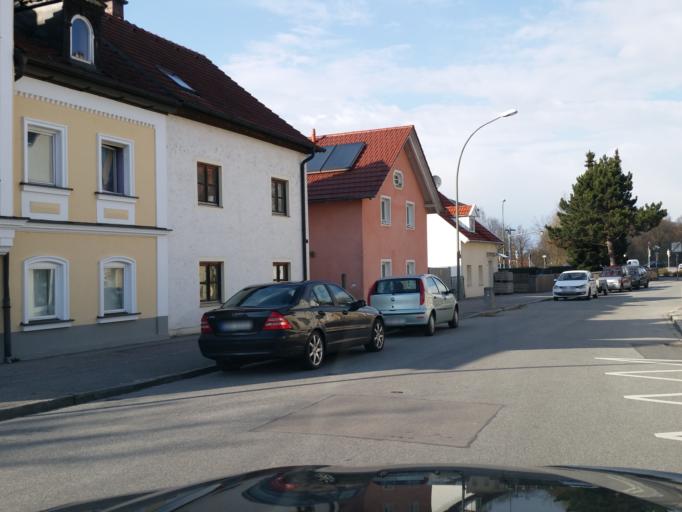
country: DE
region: Bavaria
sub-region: Lower Bavaria
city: Landshut
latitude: 48.5278
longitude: 12.1402
